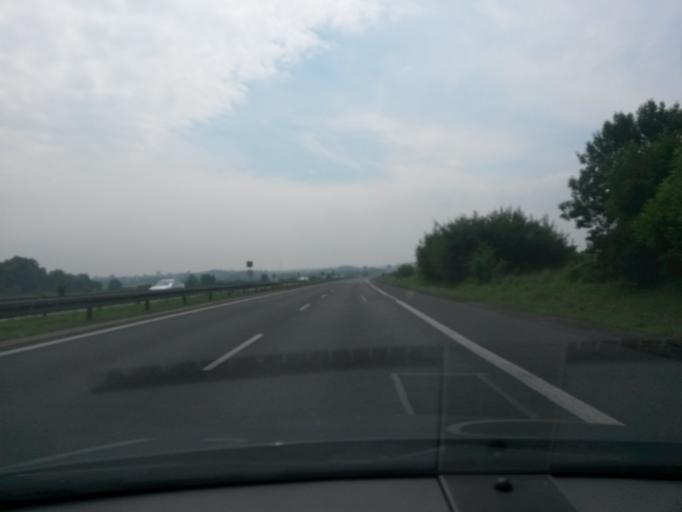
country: PL
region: Lodz Voivodeship
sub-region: Powiat piotrkowski
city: Wola Krzysztoporska
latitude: 51.3207
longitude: 19.5785
